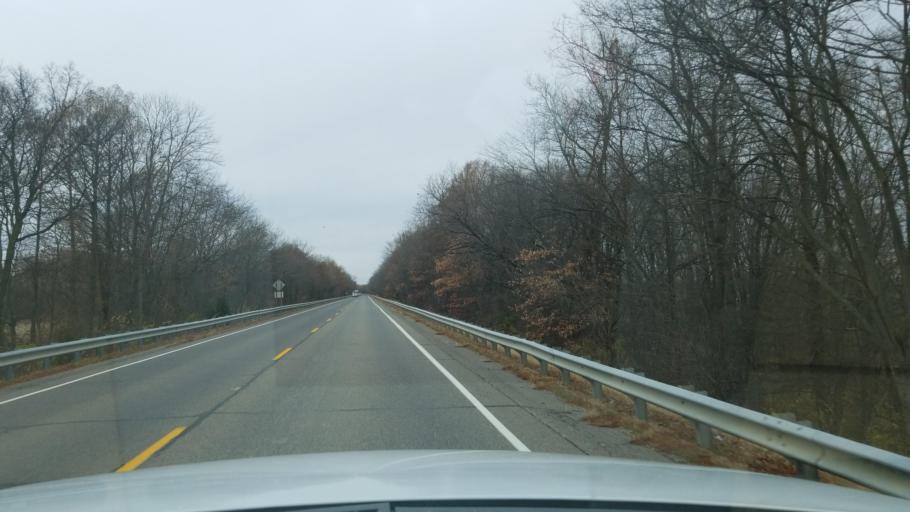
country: US
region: Indiana
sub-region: Posey County
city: Mount Vernon
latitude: 37.9342
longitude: -88.0065
